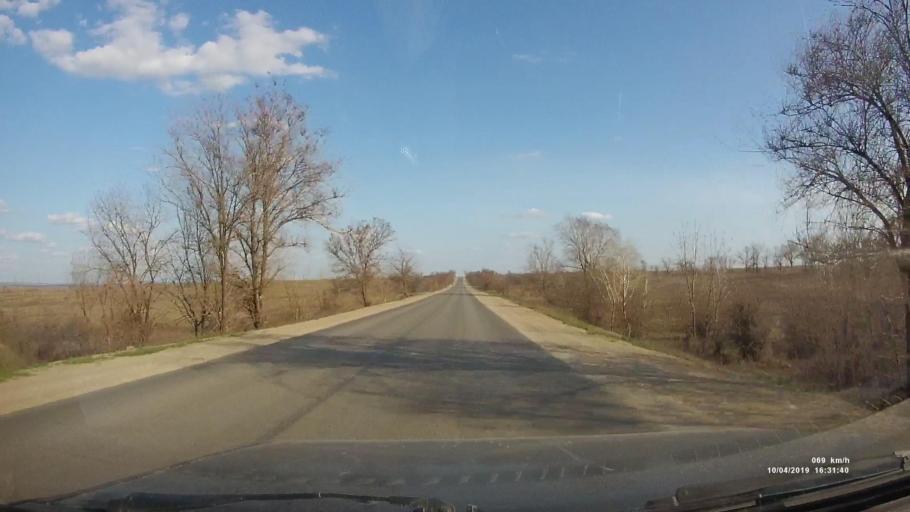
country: RU
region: Rostov
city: Staraya Stanitsa
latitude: 48.2525
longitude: 40.3783
